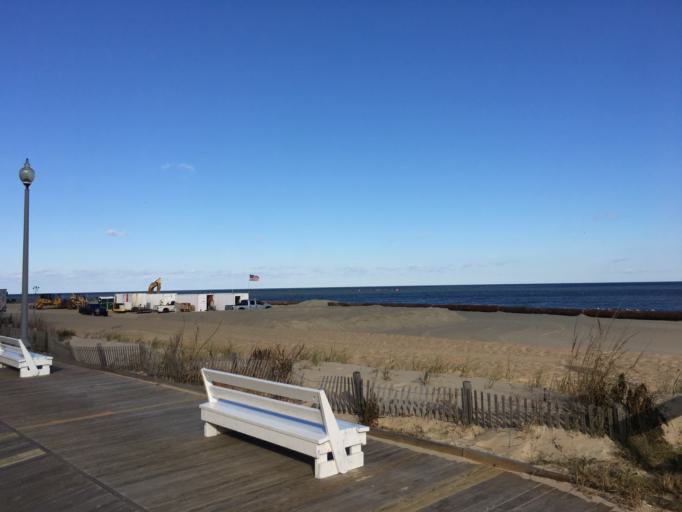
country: US
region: Delaware
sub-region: Sussex County
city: Rehoboth Beach
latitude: 38.7181
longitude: -75.0763
